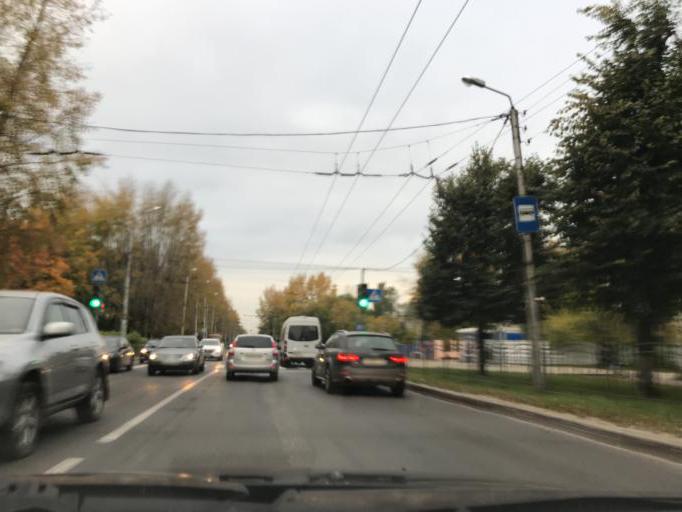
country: RU
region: Kaluga
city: Kaluga
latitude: 54.5430
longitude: 36.2697
